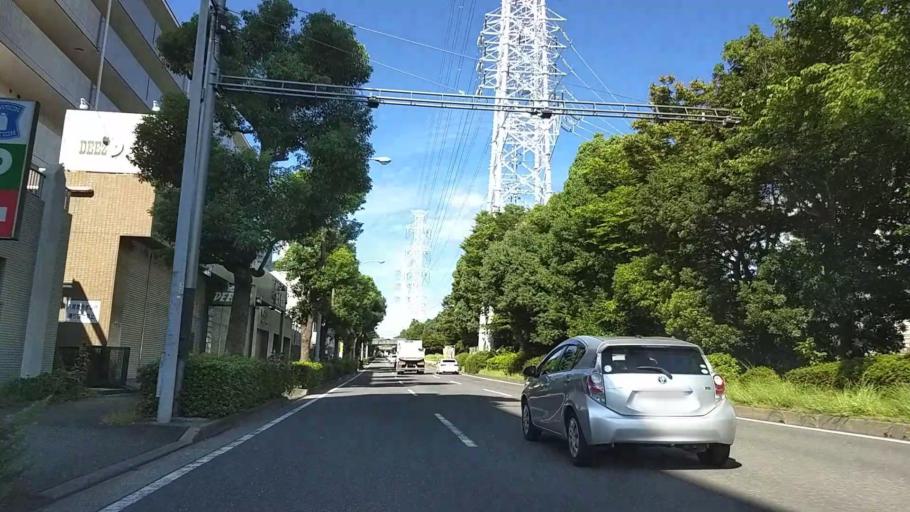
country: JP
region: Kanagawa
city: Yokohama
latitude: 35.5363
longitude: 139.5743
